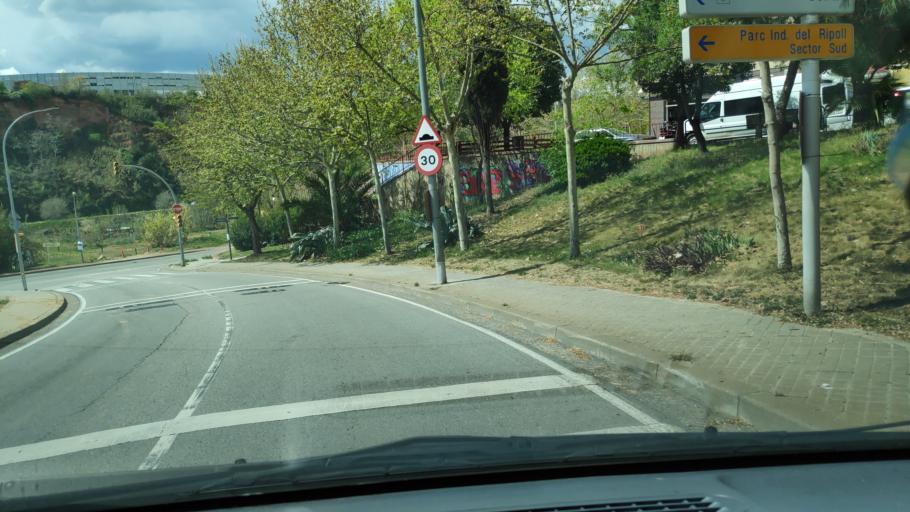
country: ES
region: Catalonia
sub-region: Provincia de Barcelona
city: Sabadell
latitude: 41.5477
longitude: 2.1239
